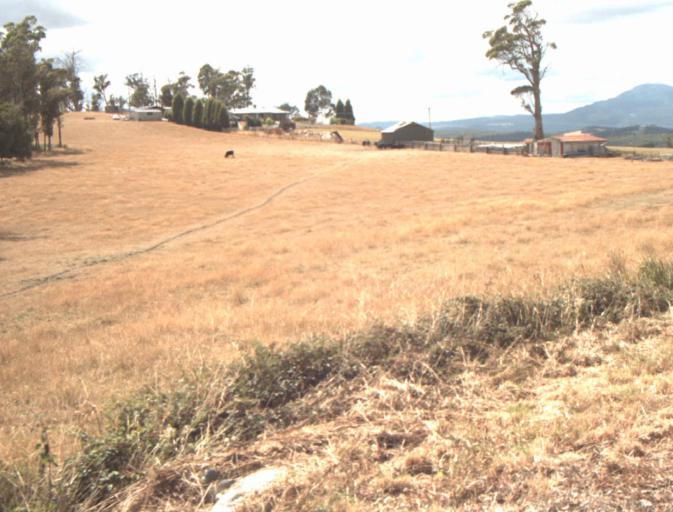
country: AU
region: Tasmania
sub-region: Launceston
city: Mayfield
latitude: -41.2040
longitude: 147.0945
